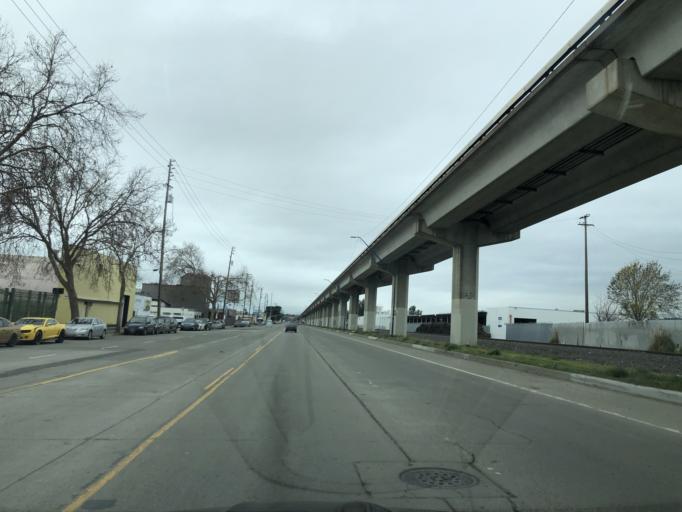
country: US
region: California
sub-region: Alameda County
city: San Leandro
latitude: 37.7443
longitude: -122.1857
